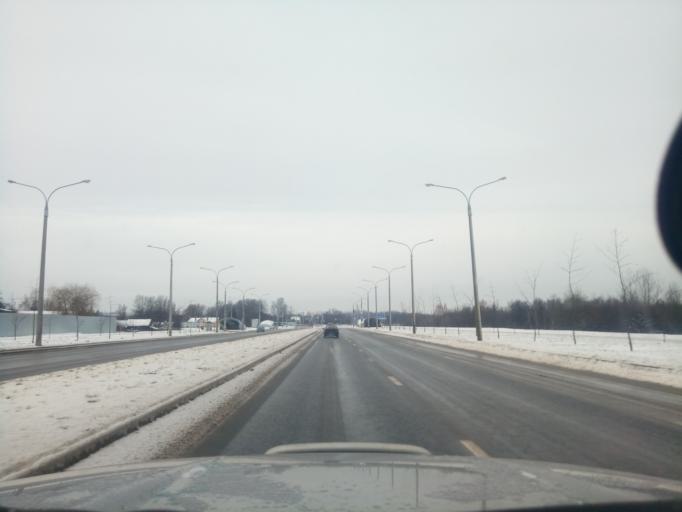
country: BY
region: Minsk
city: Machulishchy
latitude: 53.8393
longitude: 27.5954
